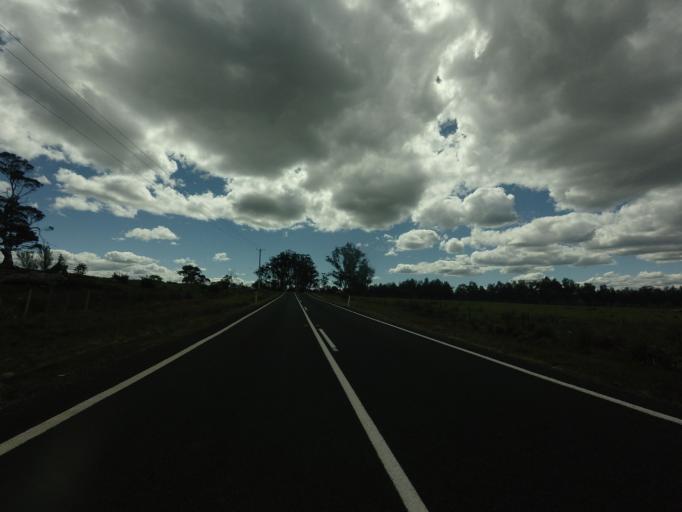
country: AU
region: Tasmania
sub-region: Northern Midlands
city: Evandale
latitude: -41.9887
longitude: 147.6746
